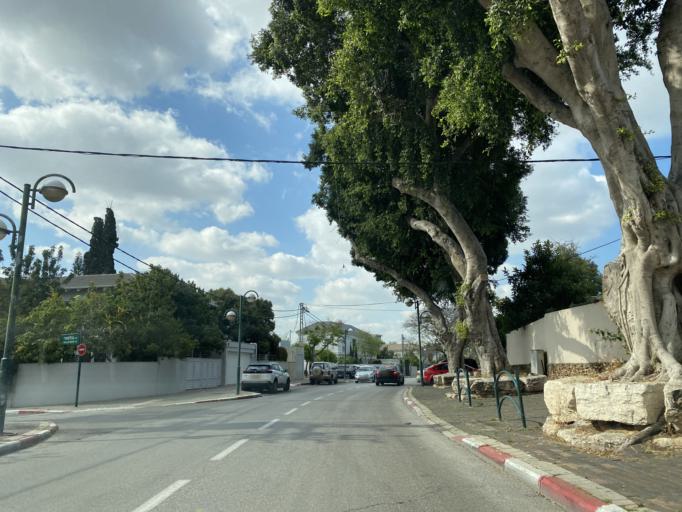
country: IL
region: Tel Aviv
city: Ramat HaSharon
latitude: 32.1327
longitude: 34.8469
